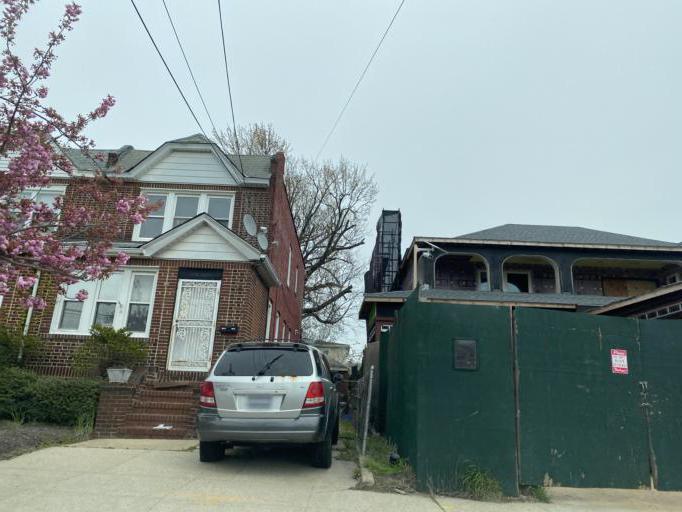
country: US
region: New York
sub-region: Queens County
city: Borough of Queens
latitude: 40.6705
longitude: -73.8267
